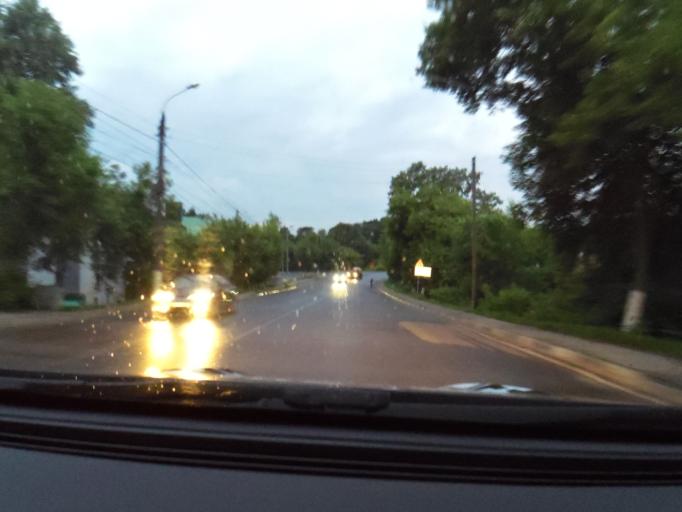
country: RU
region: Vladimir
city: Aleksandrov
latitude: 56.3987
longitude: 38.7391
